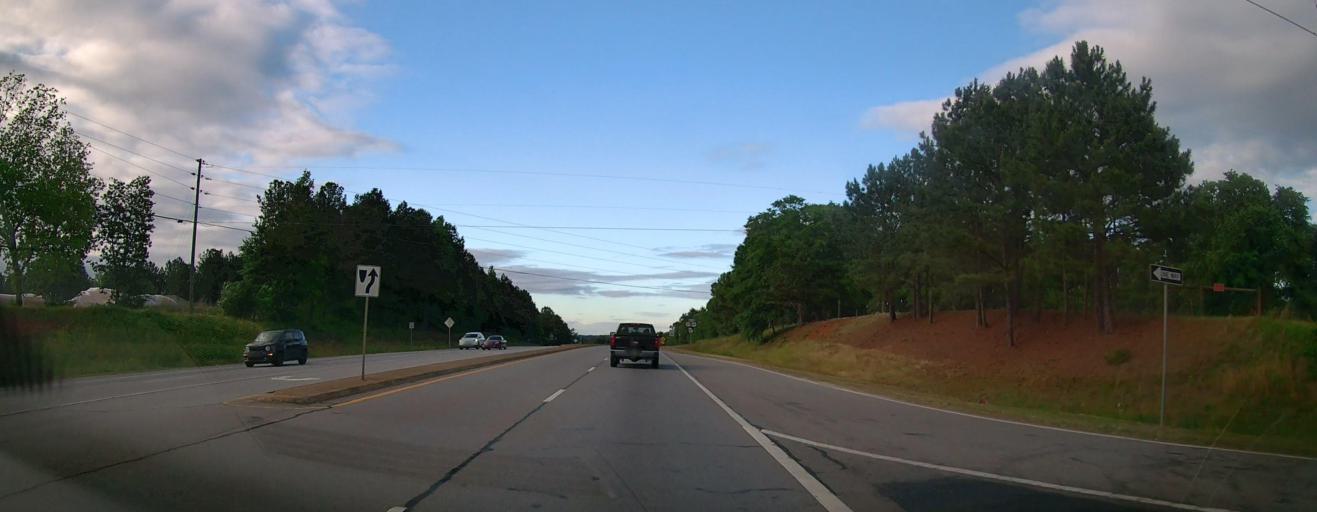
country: US
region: Georgia
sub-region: Oconee County
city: Watkinsville
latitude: 33.8926
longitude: -83.4116
